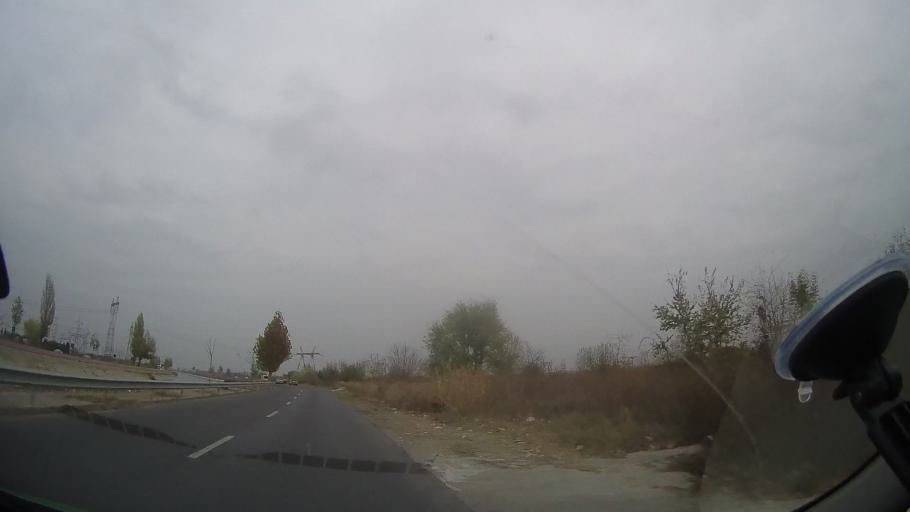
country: RO
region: Ilfov
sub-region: Comuna Popesti-Leordeni
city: Popesti-Leordeni
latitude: 44.3942
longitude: 26.1786
